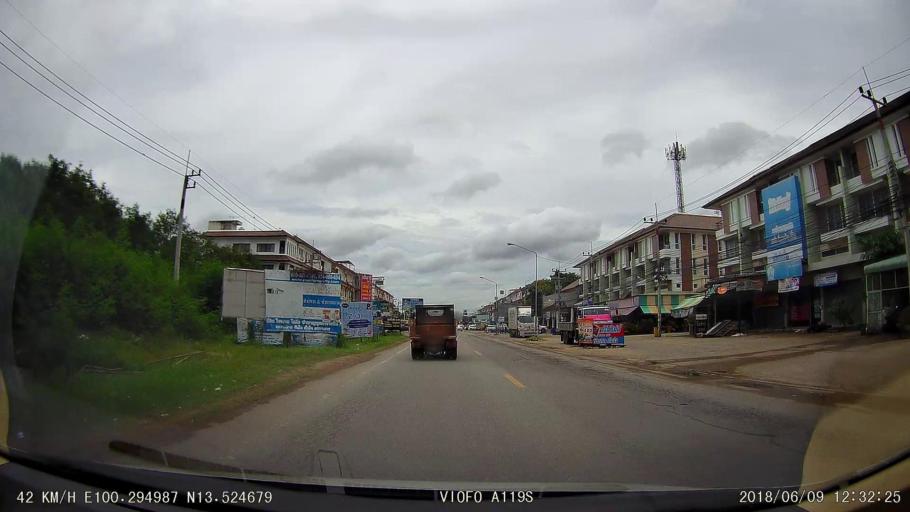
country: TH
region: Samut Sakhon
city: Samut Sakhon
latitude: 13.5246
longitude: 100.2950
